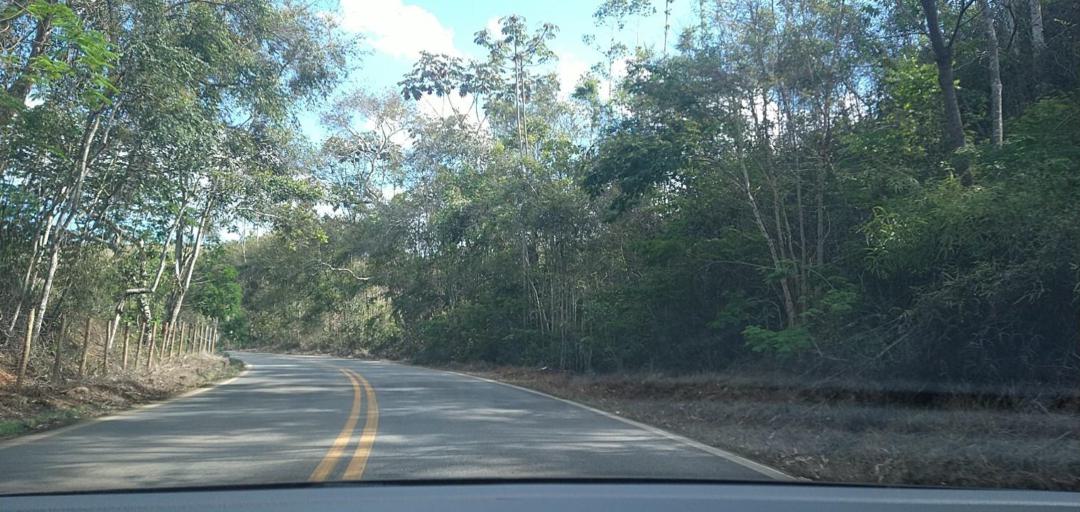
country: BR
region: Minas Gerais
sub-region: Alvinopolis
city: Alvinopolis
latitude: -20.0135
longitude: -43.0963
